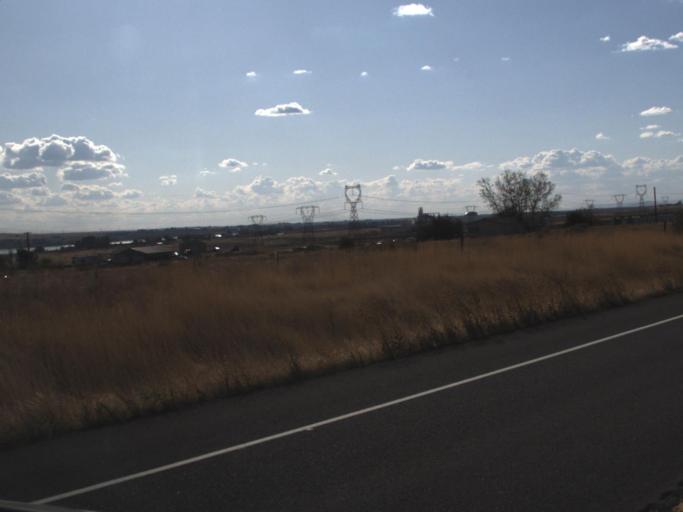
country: US
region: Oregon
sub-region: Umatilla County
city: Umatilla
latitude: 45.9452
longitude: -119.3573
